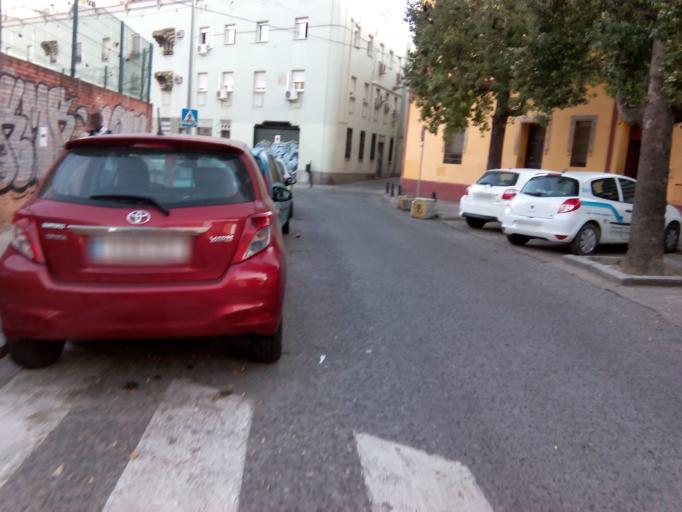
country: ES
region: Andalusia
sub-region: Provincia de Sevilla
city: Sevilla
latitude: 37.3988
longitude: -5.9839
